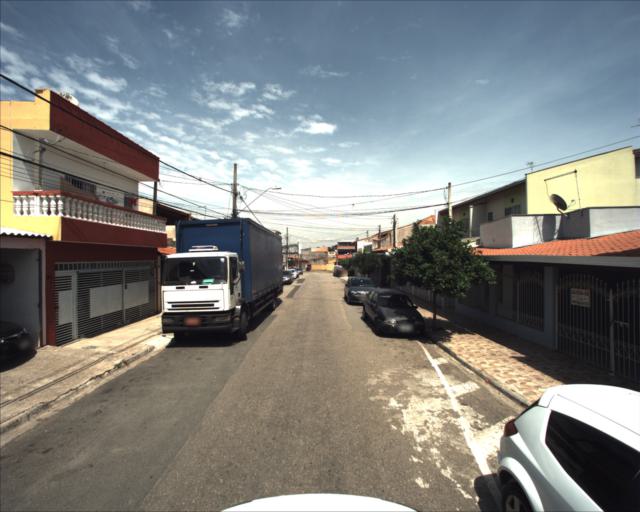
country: BR
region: Sao Paulo
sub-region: Sorocaba
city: Sorocaba
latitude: -23.4139
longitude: -47.4111
